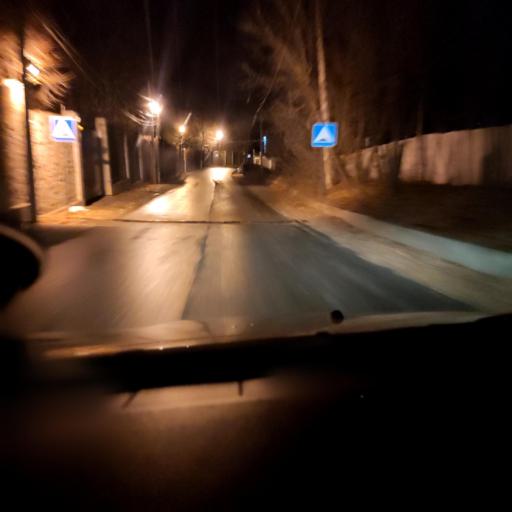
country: RU
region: Samara
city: Samara
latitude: 53.2992
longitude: 50.2085
